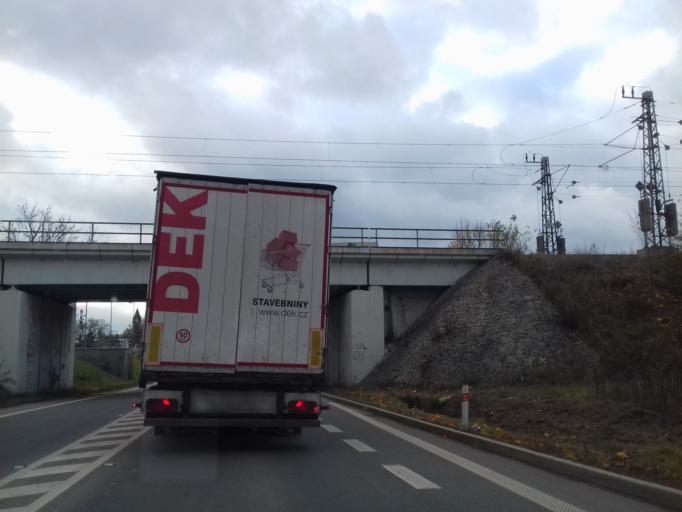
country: CZ
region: Pardubicky
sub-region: Okres Svitavy
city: Svitavy
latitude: 49.7536
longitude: 16.4793
